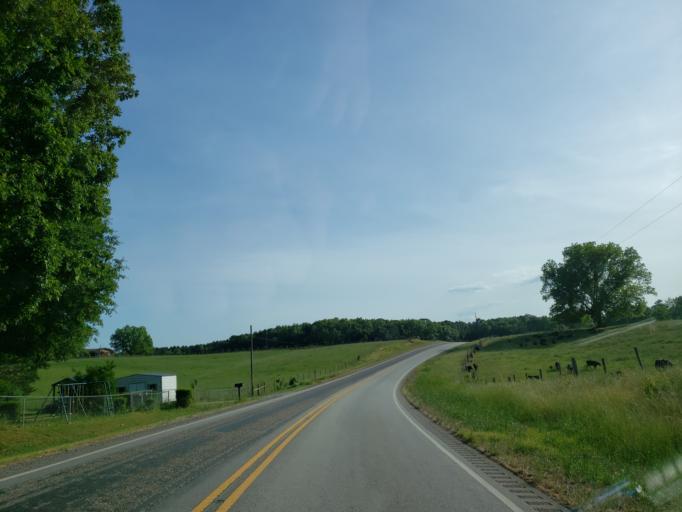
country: US
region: Georgia
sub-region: Carroll County
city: Bowdon
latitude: 33.4599
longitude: -85.3134
